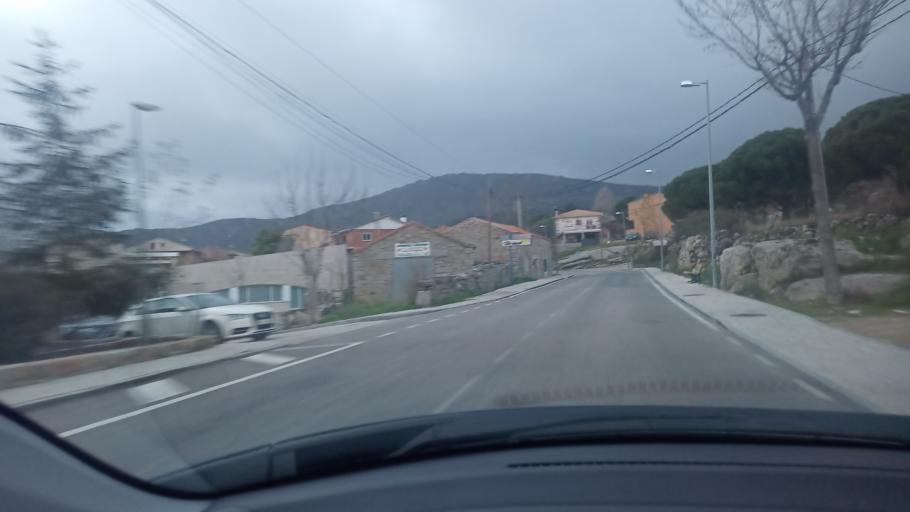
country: ES
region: Madrid
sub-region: Provincia de Madrid
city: Zarzalejo
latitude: 40.5477
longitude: -4.1786
